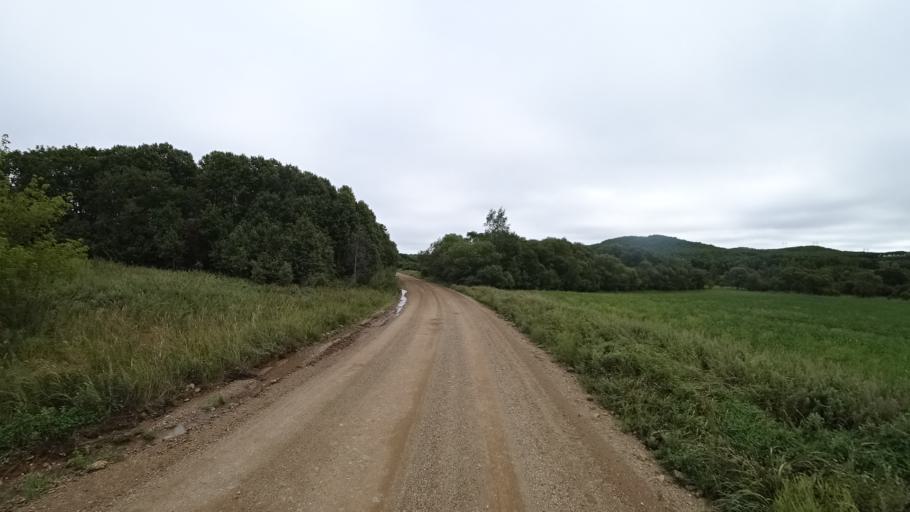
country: RU
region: Primorskiy
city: Ivanovka
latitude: 44.0572
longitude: 132.4783
